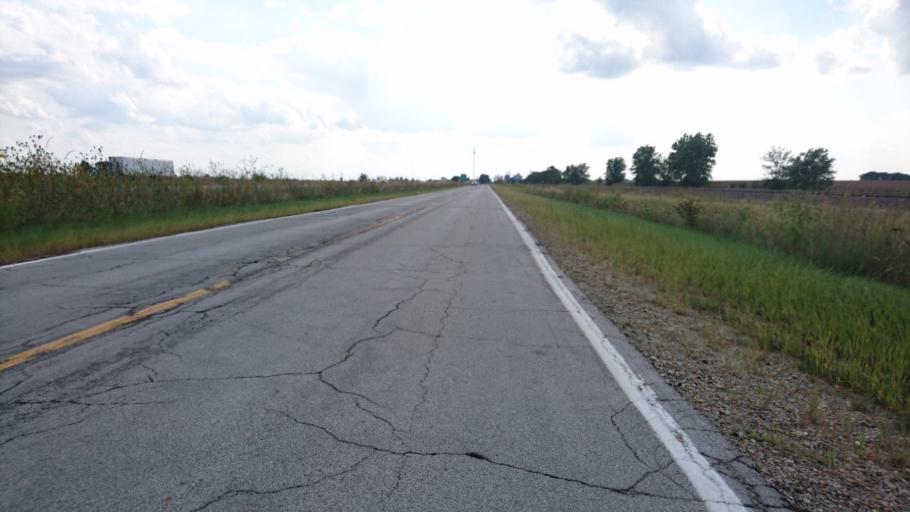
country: US
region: Illinois
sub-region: Logan County
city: Atlanta
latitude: 40.3324
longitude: -89.1485
